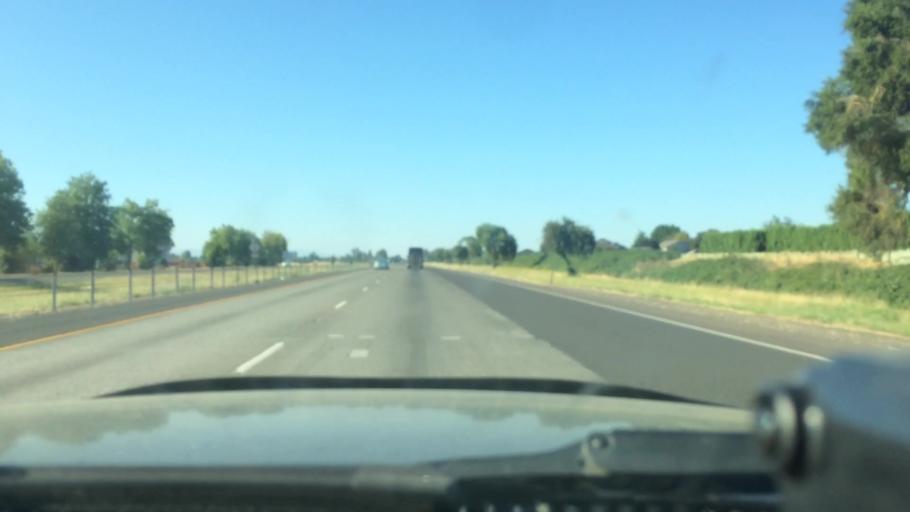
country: US
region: Oregon
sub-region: Linn County
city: Albany
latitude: 44.6255
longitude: -123.0623
